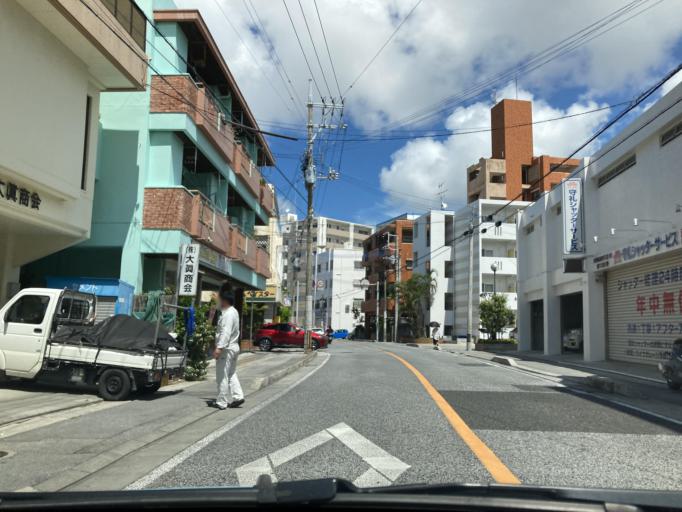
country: JP
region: Okinawa
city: Naha-shi
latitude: 26.2137
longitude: 127.6964
